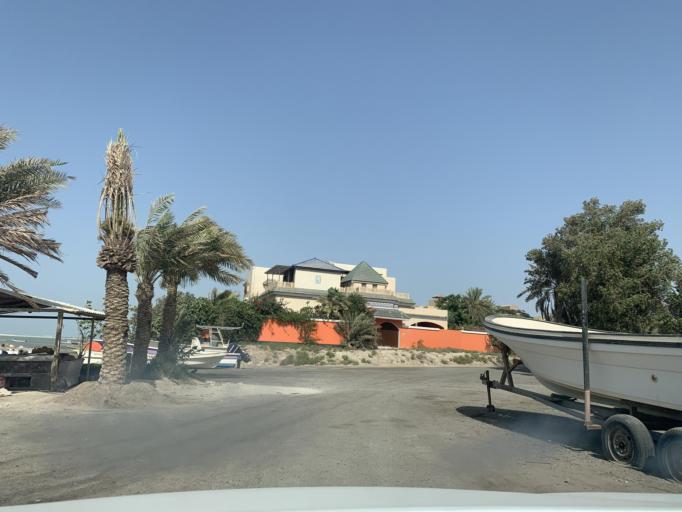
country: BH
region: Manama
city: Jidd Hafs
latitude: 26.2341
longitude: 50.4797
